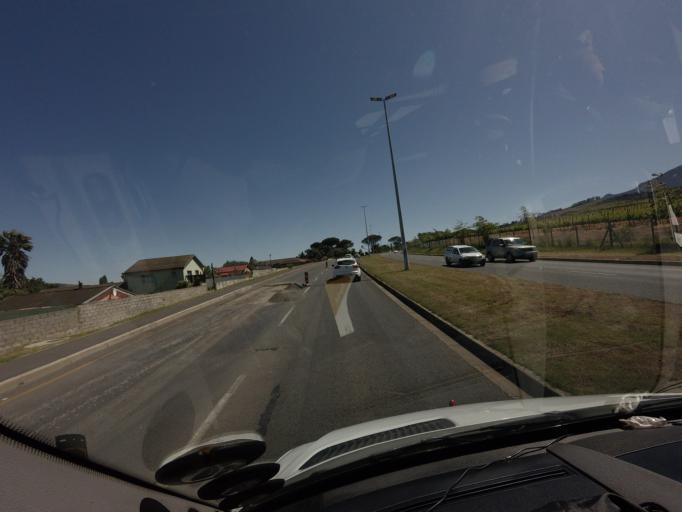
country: ZA
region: Western Cape
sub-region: Cape Winelands District Municipality
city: Stellenbosch
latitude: -33.9199
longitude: 18.8583
